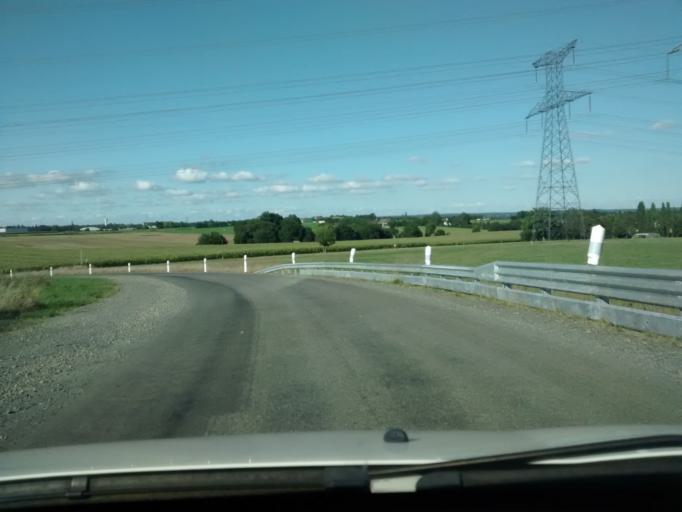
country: FR
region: Brittany
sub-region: Departement d'Ille-et-Vilaine
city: Noyal-sur-Vilaine
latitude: 48.0892
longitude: -1.5291
